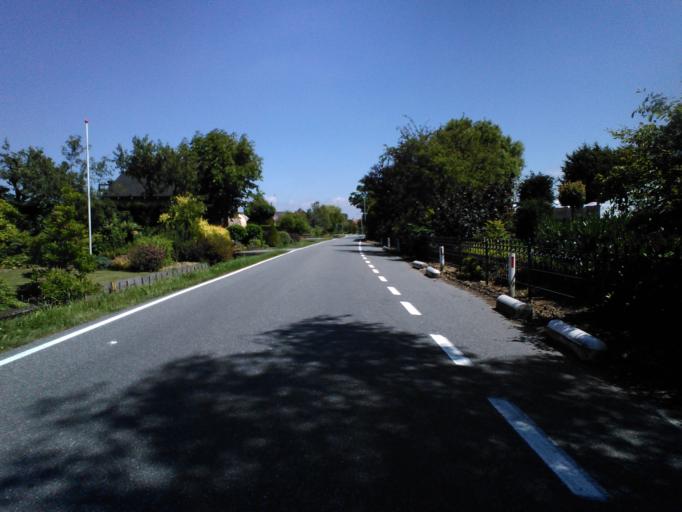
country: NL
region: South Holland
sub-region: Gemeente Westland
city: De Lier
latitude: 51.9640
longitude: 4.2387
